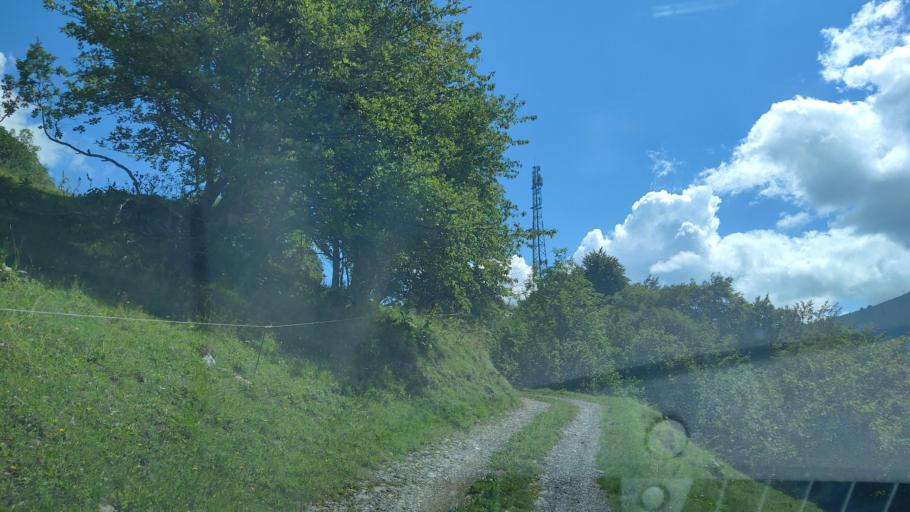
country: FR
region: Rhone-Alpes
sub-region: Departement de la Haute-Savoie
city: La Clusaz
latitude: 45.8725
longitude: 6.4843
